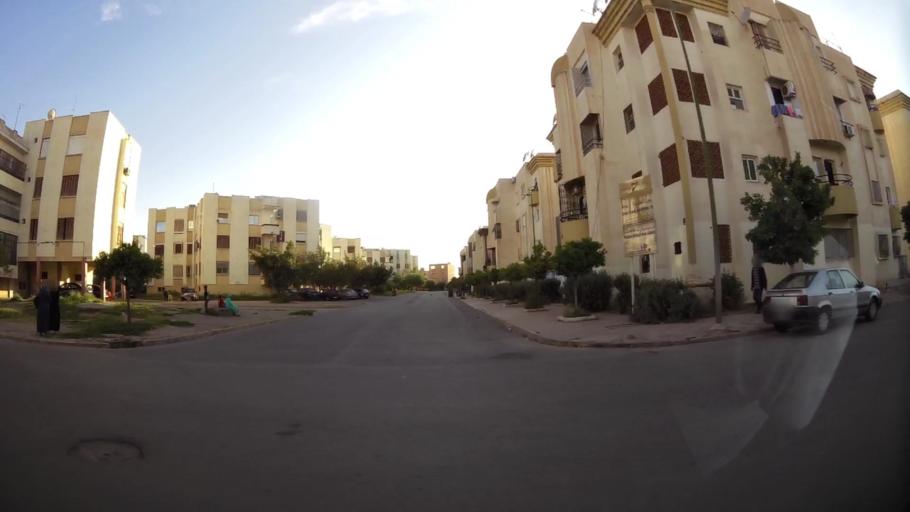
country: MA
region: Oriental
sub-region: Oujda-Angad
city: Oujda
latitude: 34.6992
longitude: -1.9142
